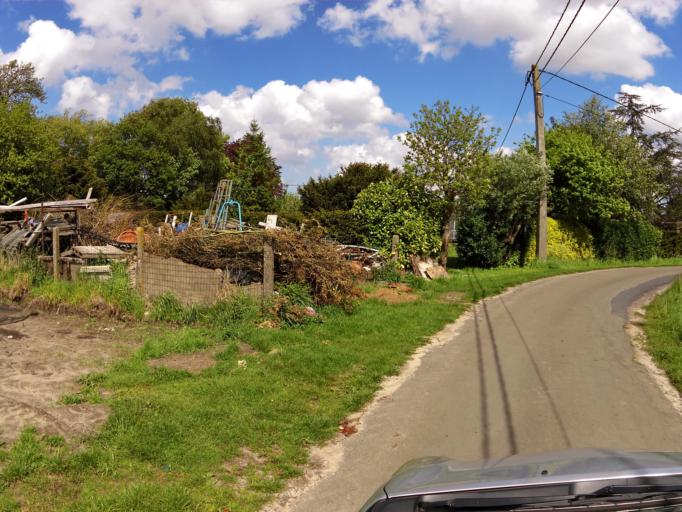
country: BE
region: Flanders
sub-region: Provincie West-Vlaanderen
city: Koekelare
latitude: 51.1156
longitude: 2.9741
